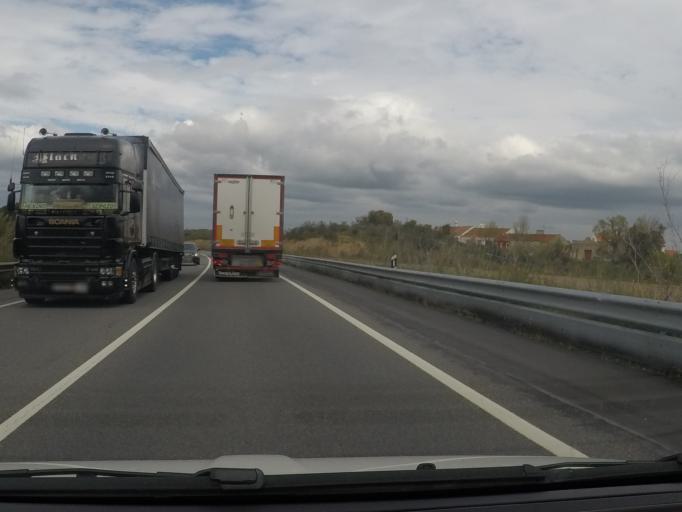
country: PT
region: Setubal
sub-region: Santiago do Cacem
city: Santiago do Cacem
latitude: 38.0733
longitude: -8.6490
